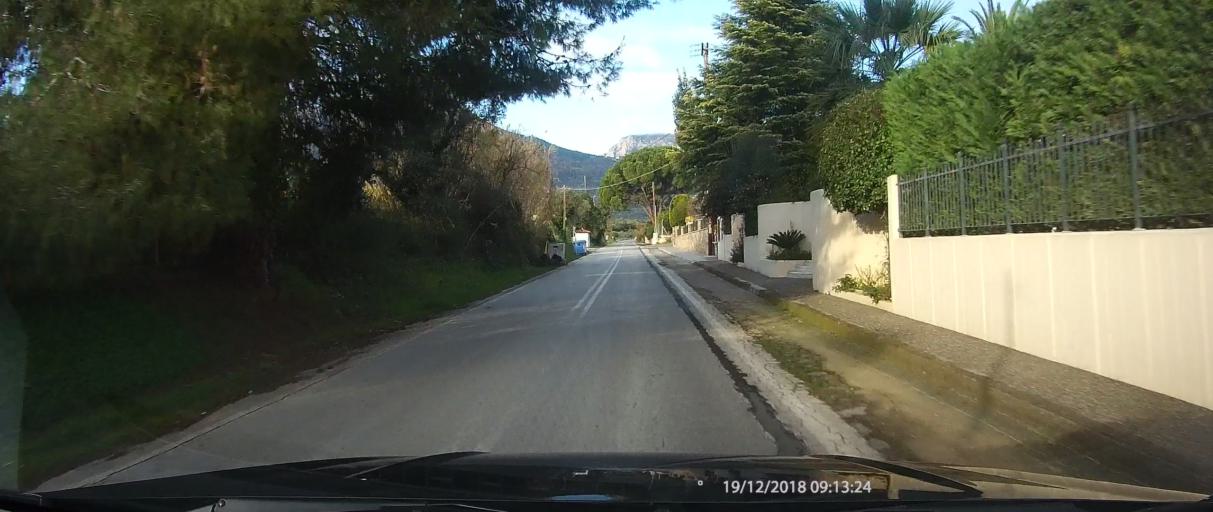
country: GR
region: Peloponnese
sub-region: Nomos Lakonias
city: Magoula
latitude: 37.0811
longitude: 22.3980
